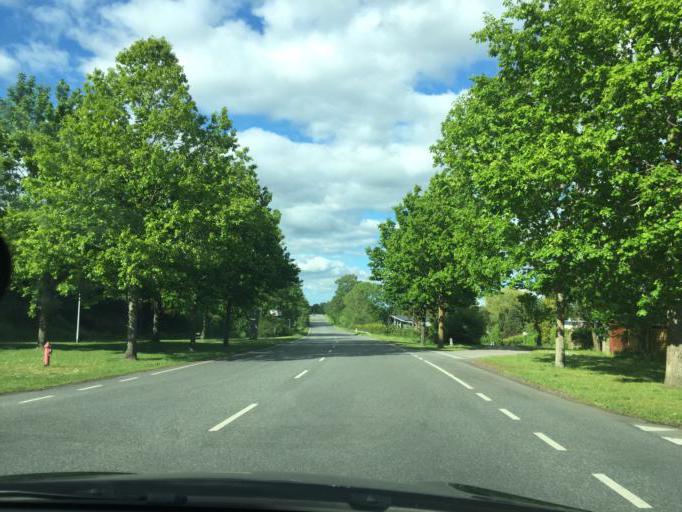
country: DK
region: South Denmark
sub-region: Odense Kommune
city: Bellinge
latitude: 55.3409
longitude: 10.3215
